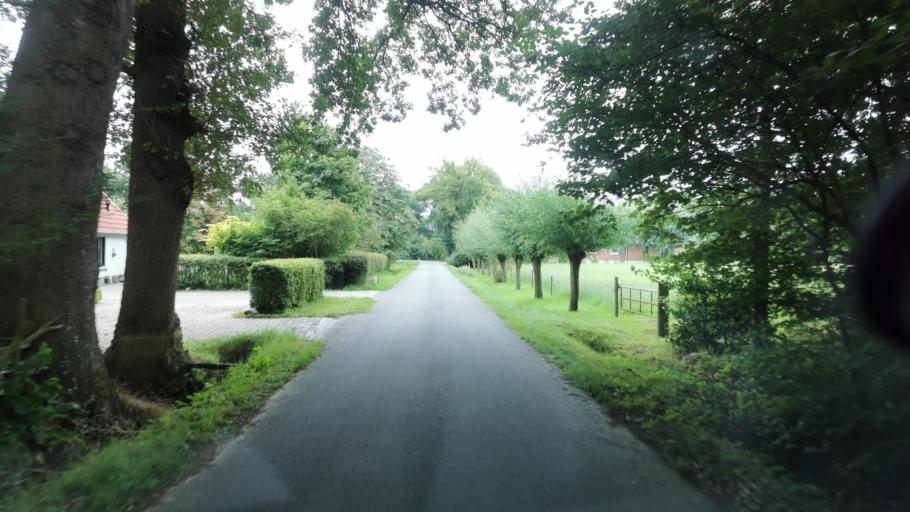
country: NL
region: Overijssel
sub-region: Gemeente Losser
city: Losser
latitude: 52.2468
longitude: 6.9748
